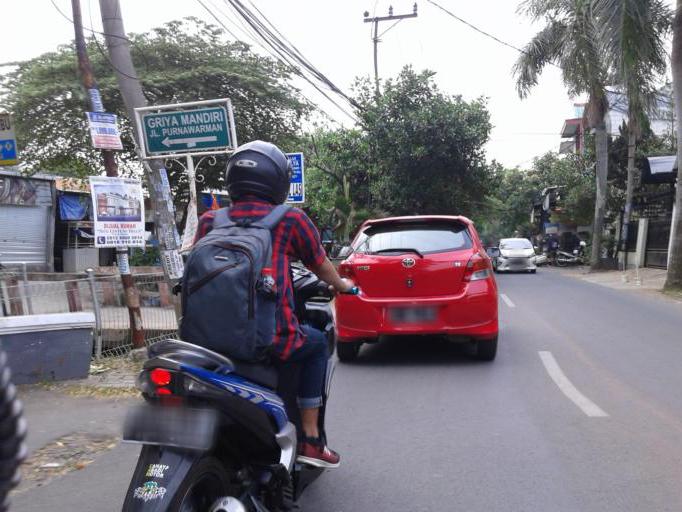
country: ID
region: West Java
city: Pamulang
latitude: -6.3225
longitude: 106.7634
